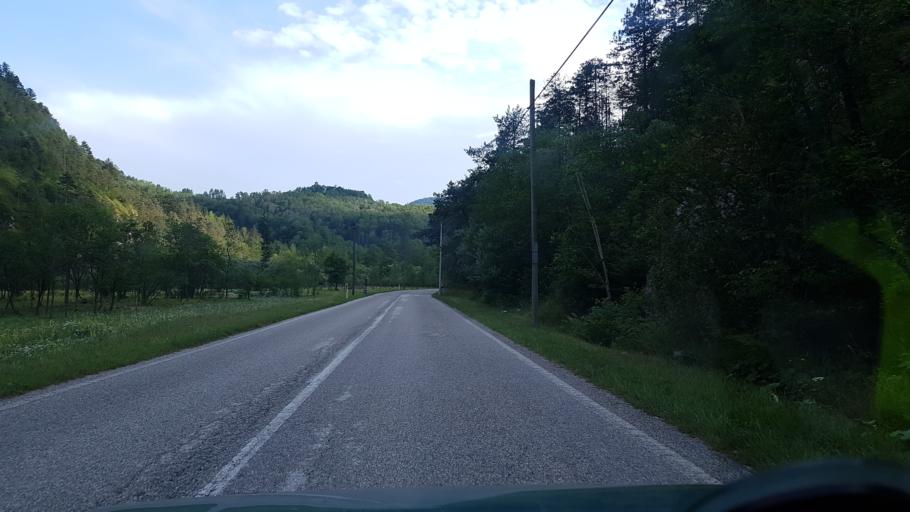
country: IT
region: Friuli Venezia Giulia
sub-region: Provincia di Udine
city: Lusevera
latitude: 46.2891
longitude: 13.2678
